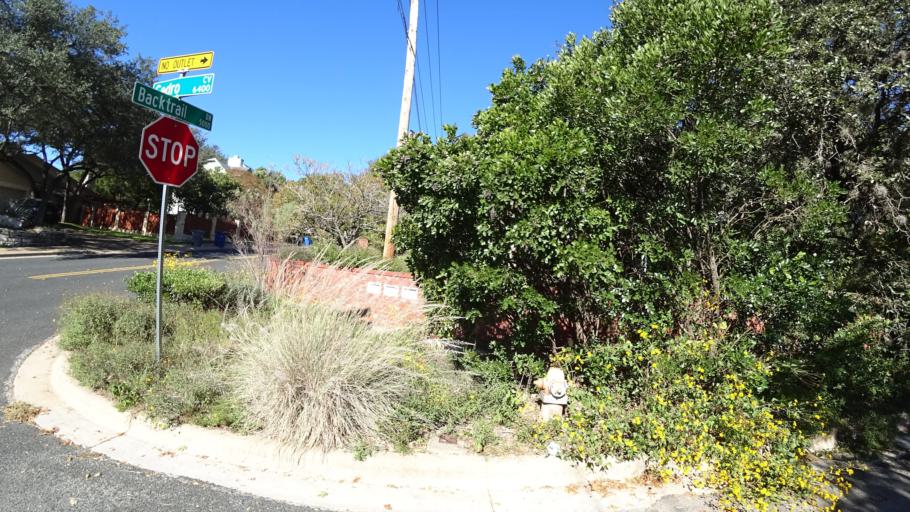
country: US
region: Texas
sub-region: Travis County
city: West Lake Hills
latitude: 30.3599
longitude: -97.7820
